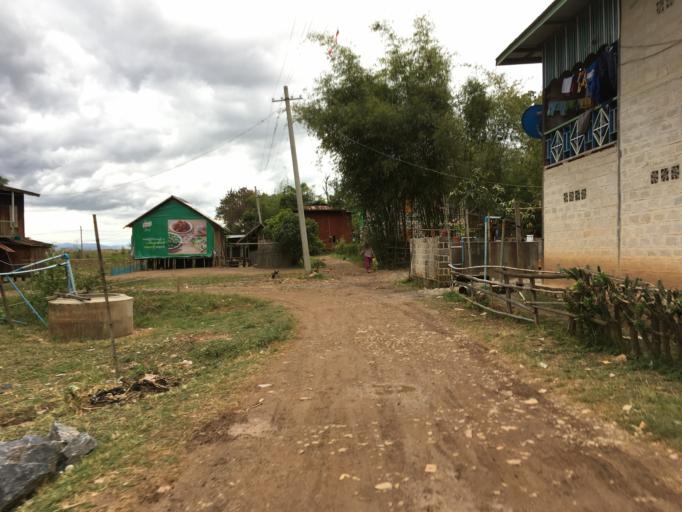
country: MM
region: Shan
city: Taunggyi
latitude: 20.6193
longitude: 96.8838
